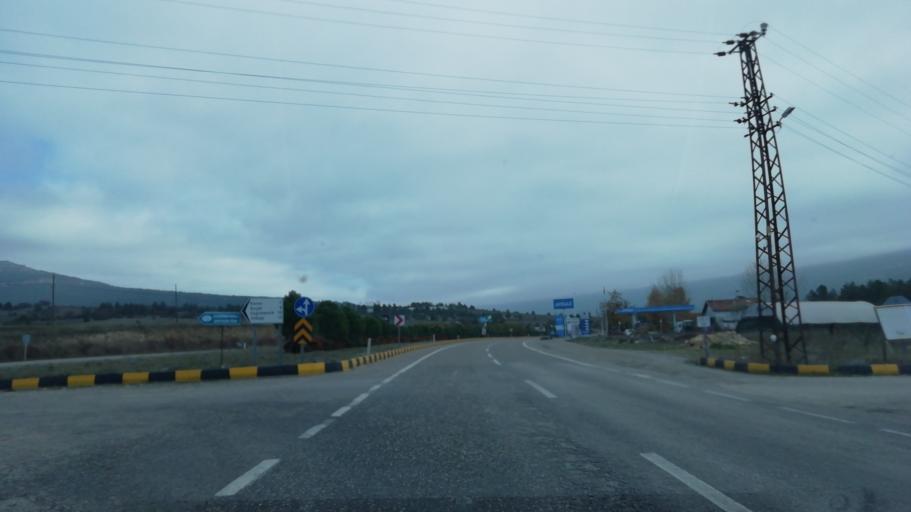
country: TR
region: Karabuk
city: Safranbolu
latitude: 41.2222
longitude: 32.7819
